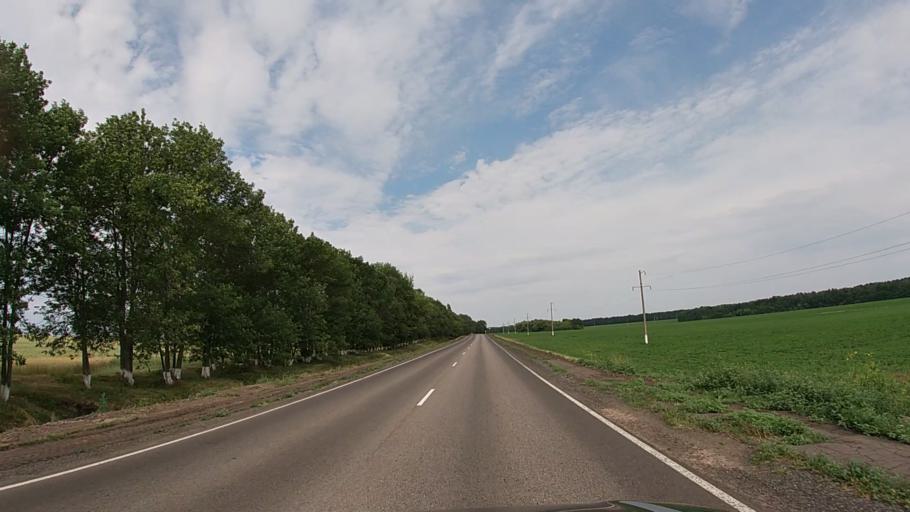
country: RU
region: Belgorod
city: Krasnaya Yaruga
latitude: 50.8098
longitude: 35.5185
